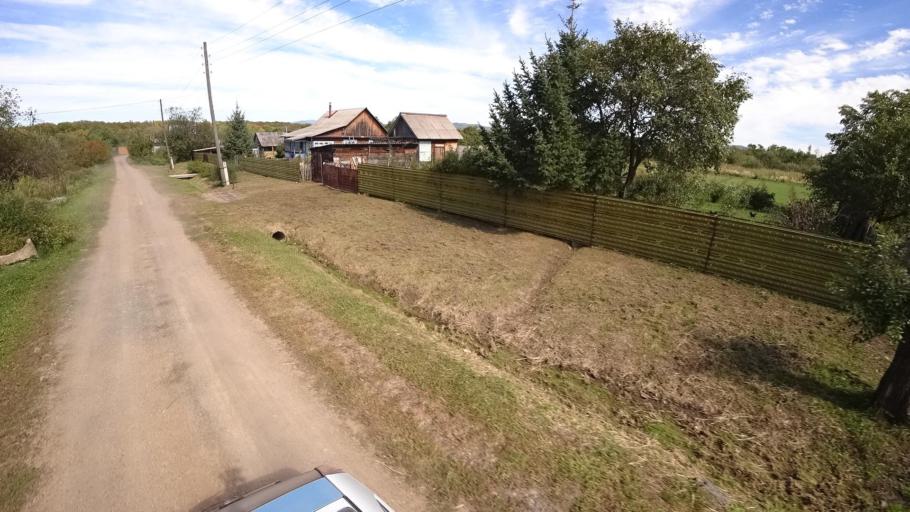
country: RU
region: Primorskiy
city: Yakovlevka
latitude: 44.4361
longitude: 133.5607
